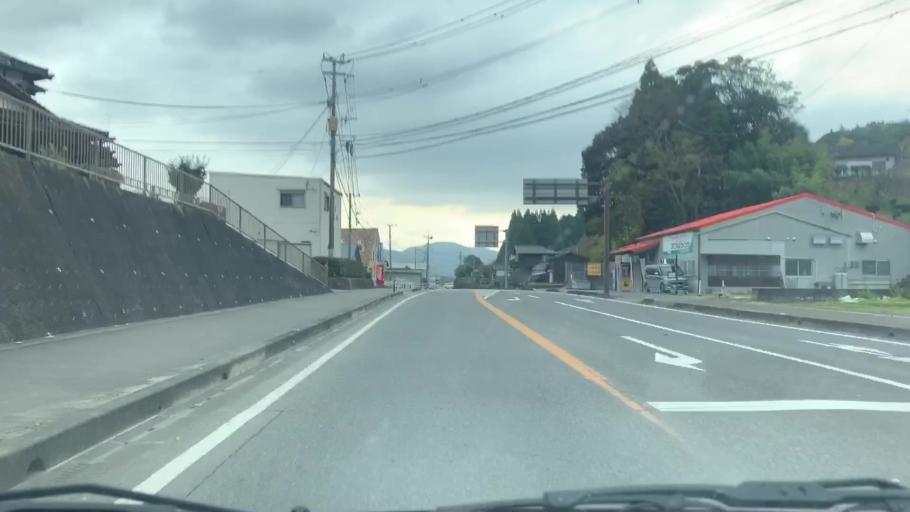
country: JP
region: Saga Prefecture
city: Takeocho-takeo
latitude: 33.1838
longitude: 130.0396
